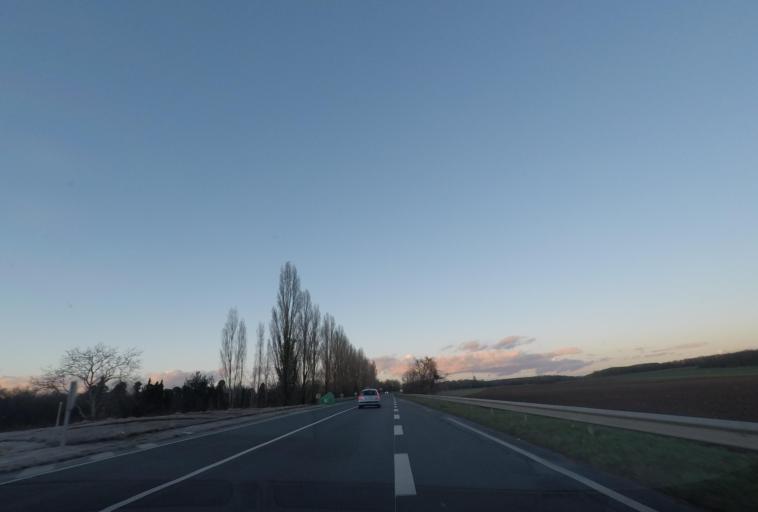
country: FR
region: Ile-de-France
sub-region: Departement de l'Essonne
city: Vert-le-Grand
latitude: 48.5722
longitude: 2.3644
